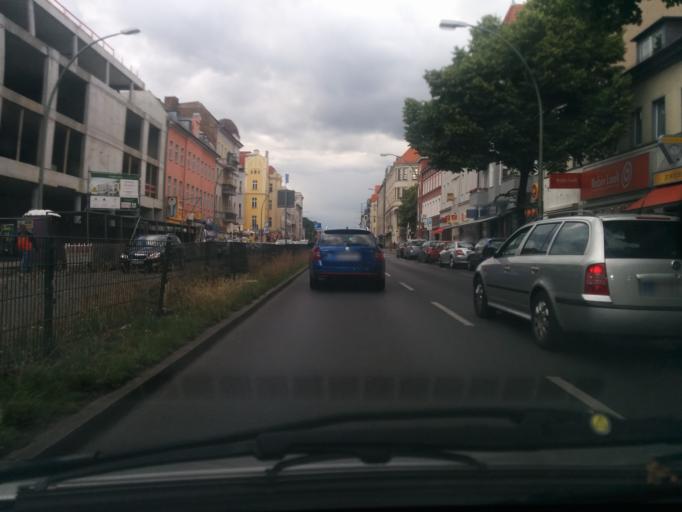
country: DE
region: Berlin
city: Tempelhof Bezirk
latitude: 52.4583
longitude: 13.3843
